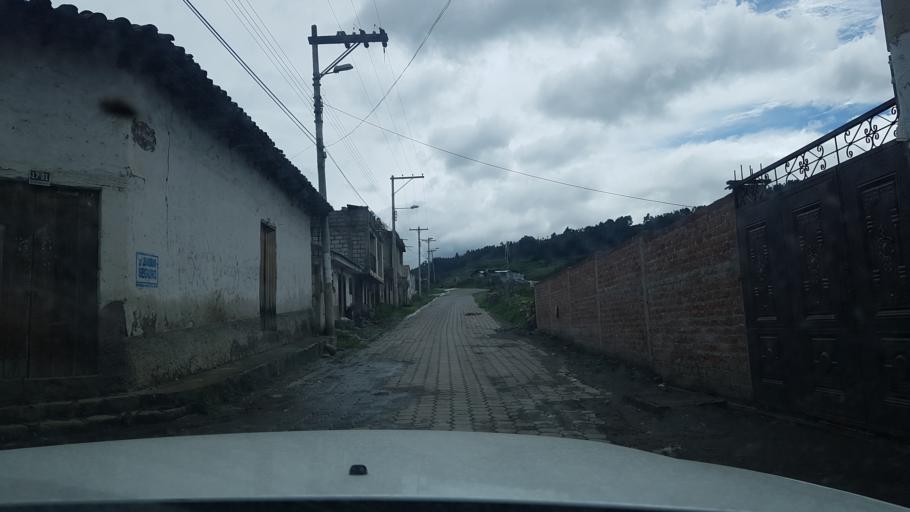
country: EC
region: Chimborazo
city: Riobamba
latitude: -1.7036
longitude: -78.7770
